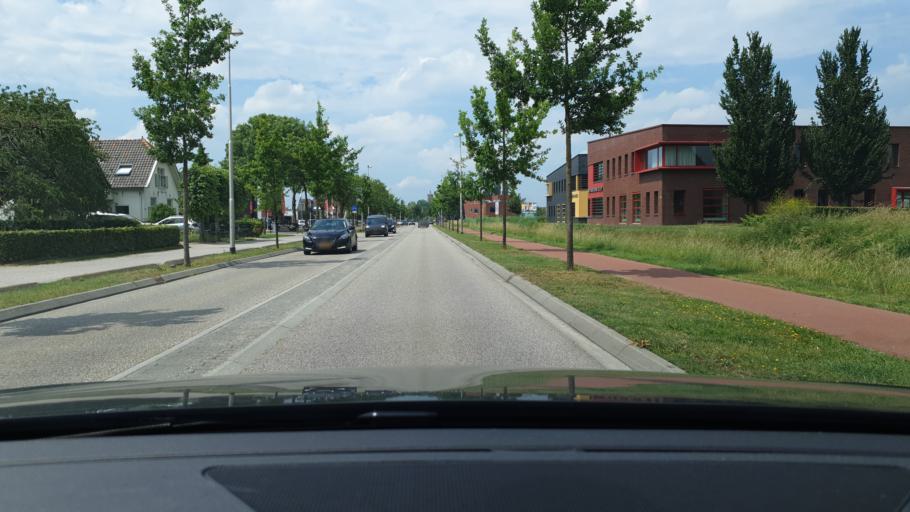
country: NL
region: Gelderland
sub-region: Gemeente Overbetuwe
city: Elst
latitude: 51.9155
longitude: 5.8656
